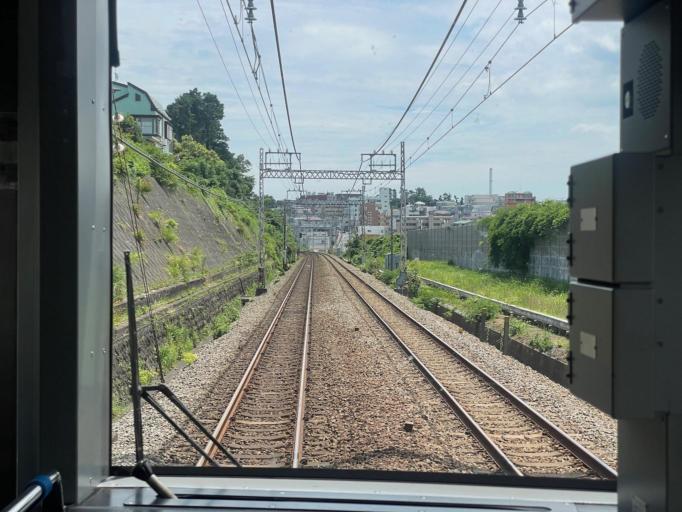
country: JP
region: Kanagawa
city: Fujisawa
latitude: 35.3686
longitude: 139.4729
